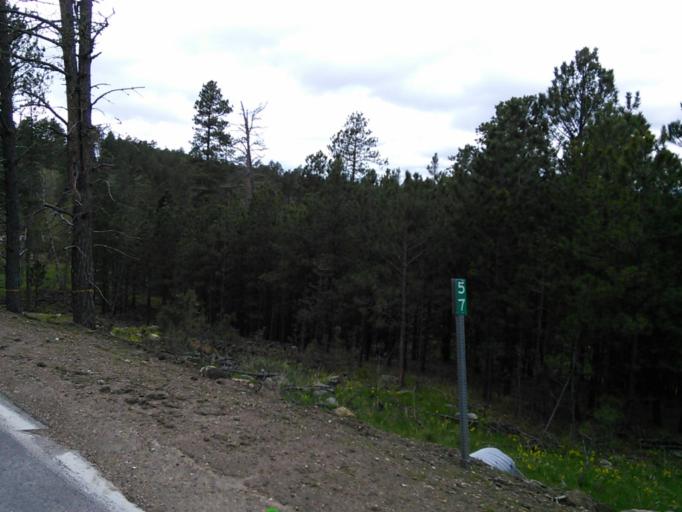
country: US
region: South Dakota
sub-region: Custer County
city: Custer
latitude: 43.7517
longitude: -103.4810
